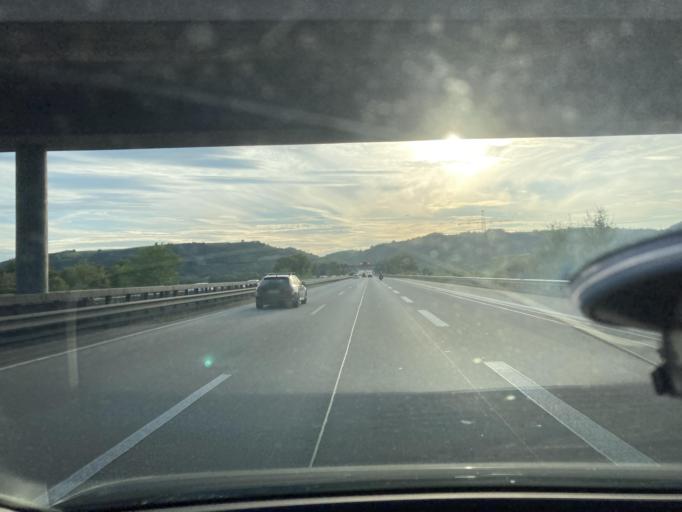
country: DE
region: Rheinland-Pfalz
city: Laubenheim
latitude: 49.9318
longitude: 7.9106
